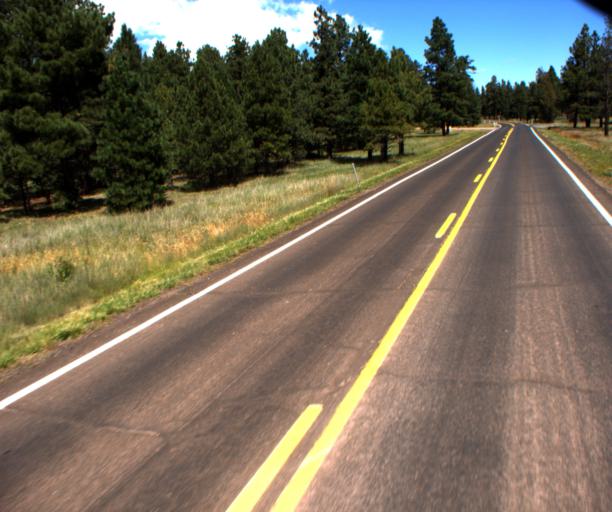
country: US
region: Arizona
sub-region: Apache County
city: Eagar
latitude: 34.0325
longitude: -109.4518
